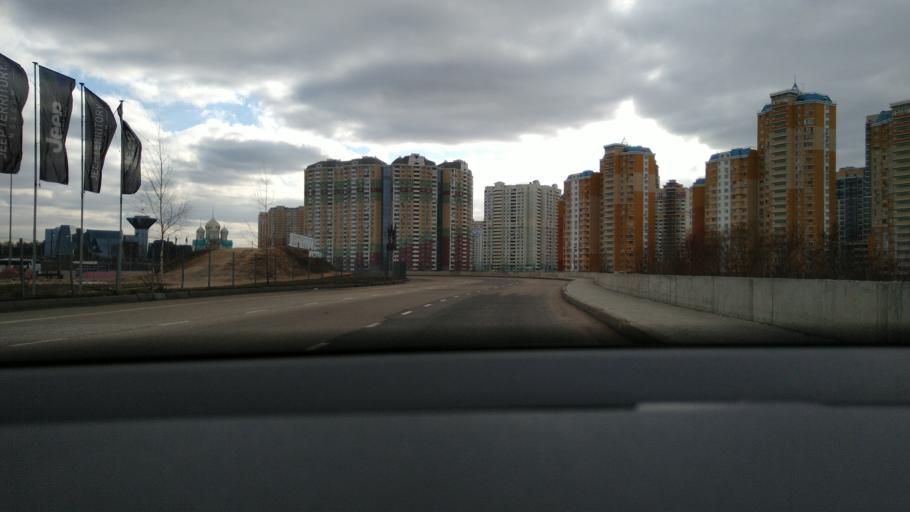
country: RU
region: Moskovskaya
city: Pavshino
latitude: 55.8277
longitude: 37.3802
